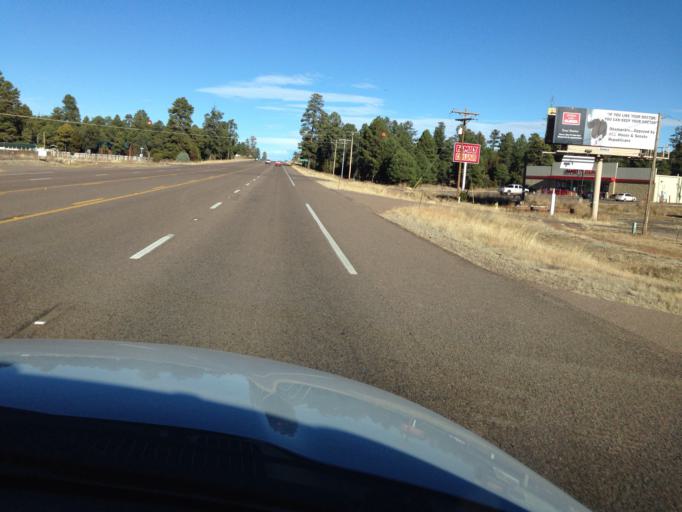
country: US
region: Arizona
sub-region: Navajo County
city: Heber-Overgaard
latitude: 34.4056
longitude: -110.5658
